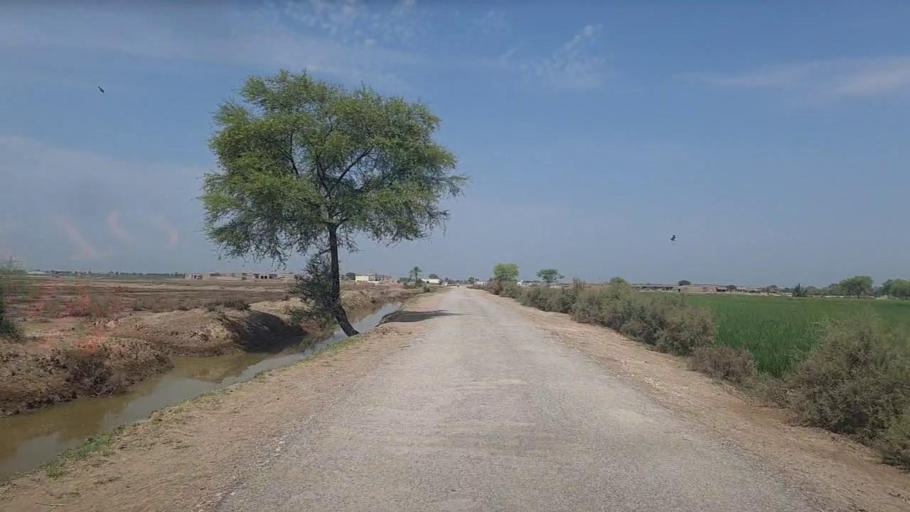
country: PK
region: Sindh
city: Thul
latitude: 28.2895
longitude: 68.6838
